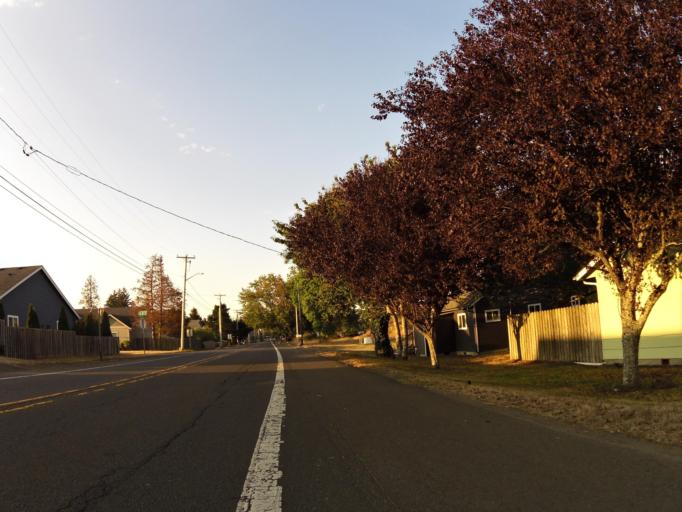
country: US
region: Oregon
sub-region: Clatsop County
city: Warrenton
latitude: 46.1509
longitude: -123.9279
